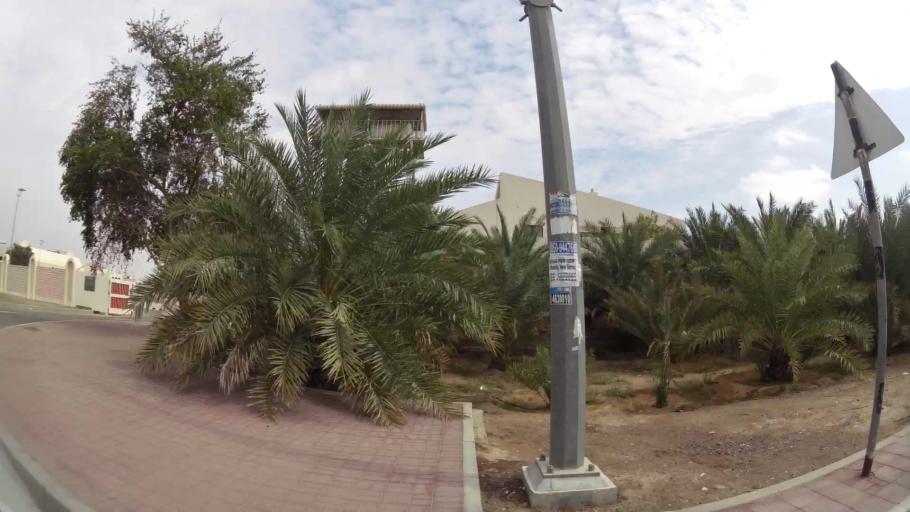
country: AE
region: Abu Dhabi
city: Al Ain
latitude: 24.2033
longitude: 55.7947
